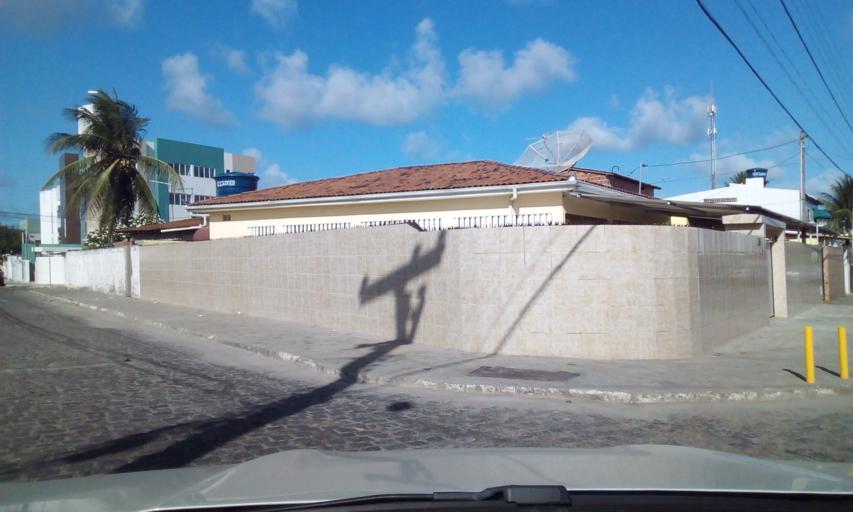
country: BR
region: Paraiba
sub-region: Joao Pessoa
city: Joao Pessoa
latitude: -7.1741
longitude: -34.8390
